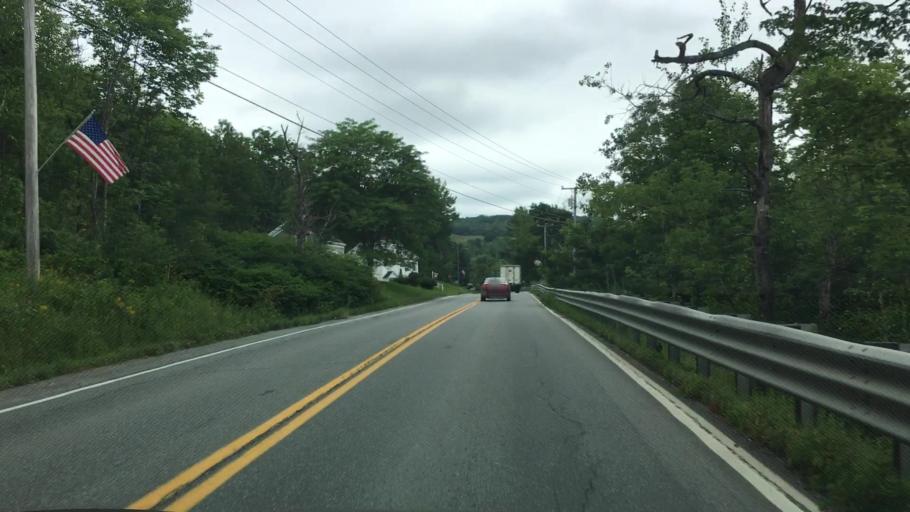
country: US
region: Maine
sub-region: Waldo County
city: Frankfort
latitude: 44.6044
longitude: -68.8707
